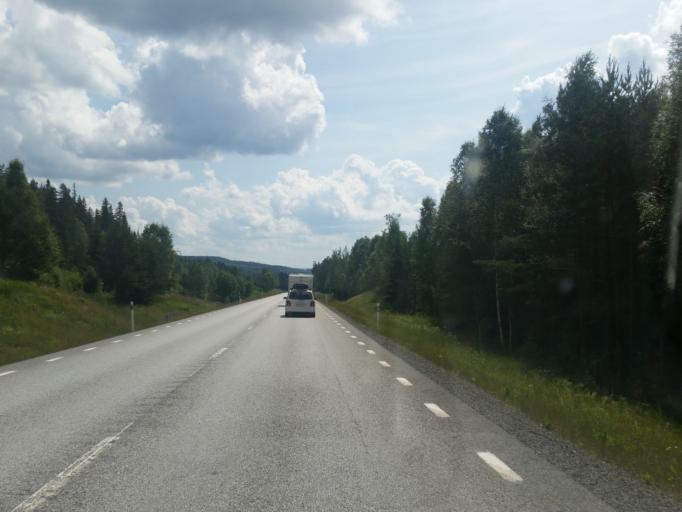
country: SE
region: OErebro
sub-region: Ljusnarsbergs Kommun
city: Kopparberg
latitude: 59.8828
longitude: 15.0263
